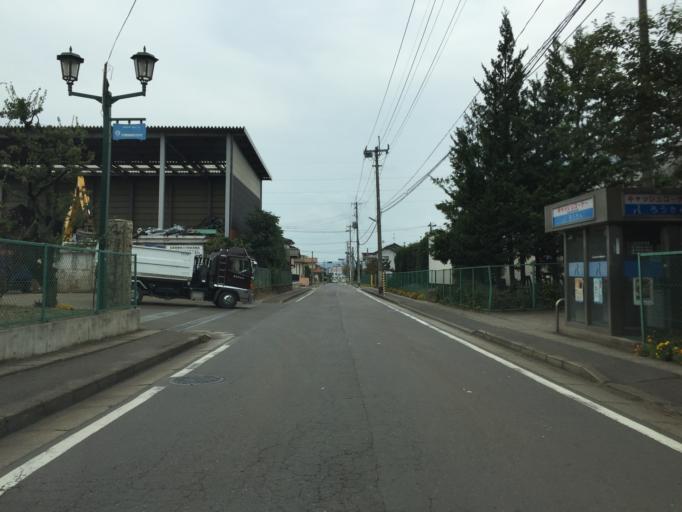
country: JP
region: Fukushima
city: Fukushima-shi
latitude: 37.7639
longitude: 140.4279
